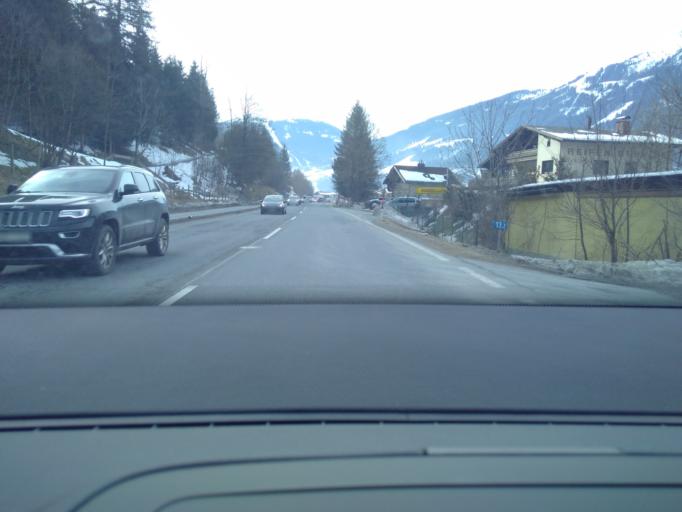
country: AT
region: Salzburg
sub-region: Politischer Bezirk Sankt Johann im Pongau
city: Bad Hofgastein
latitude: 47.1892
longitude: 13.1015
